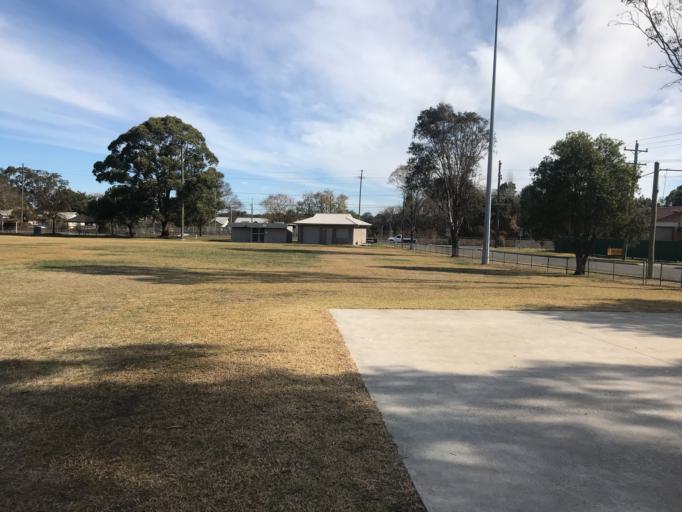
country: AU
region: New South Wales
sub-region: Blacktown
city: Riverstone
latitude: -33.6753
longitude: 150.8601
